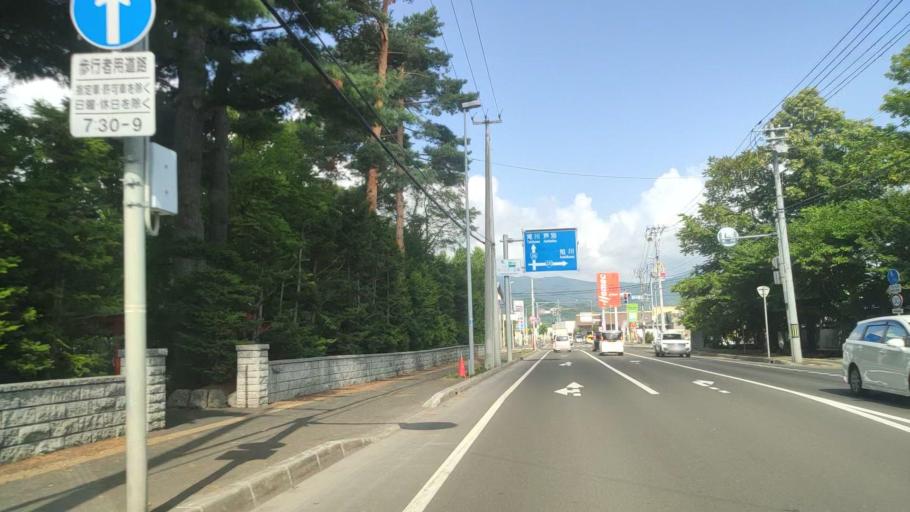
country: JP
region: Hokkaido
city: Shimo-furano
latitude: 43.3440
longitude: 142.3822
